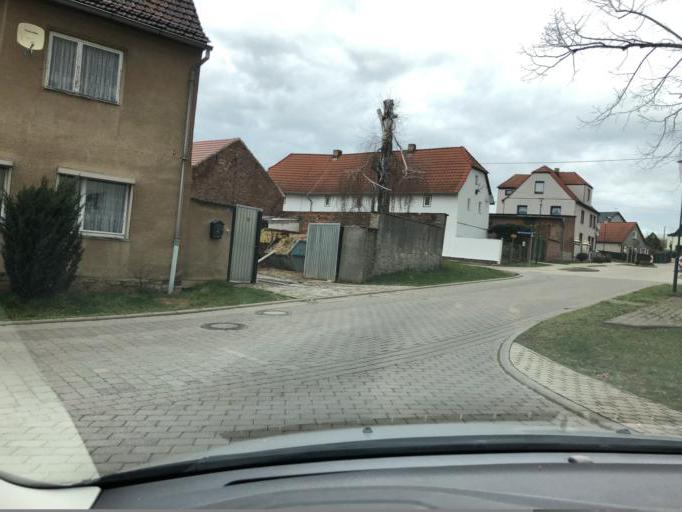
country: DE
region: Saxony-Anhalt
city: Muschwitz
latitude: 51.1899
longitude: 12.1313
